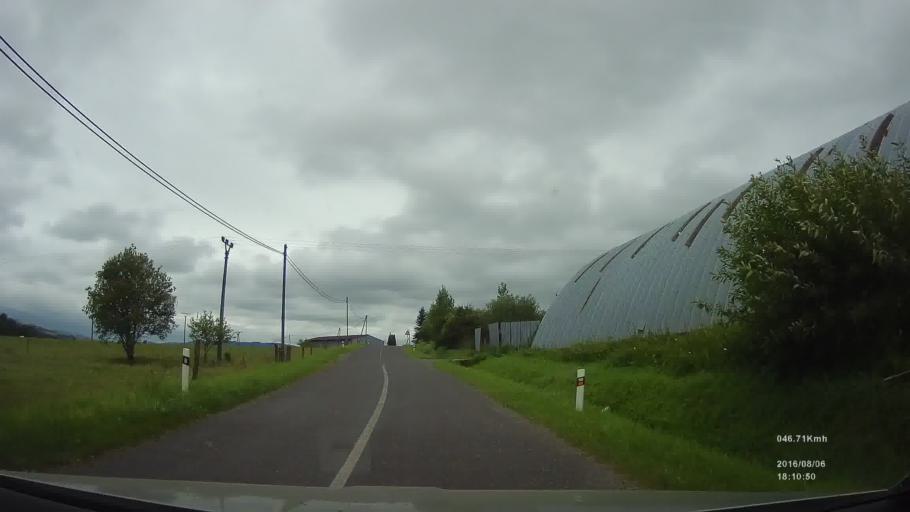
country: SK
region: Presovsky
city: Svidnik
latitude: 49.3675
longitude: 21.5752
